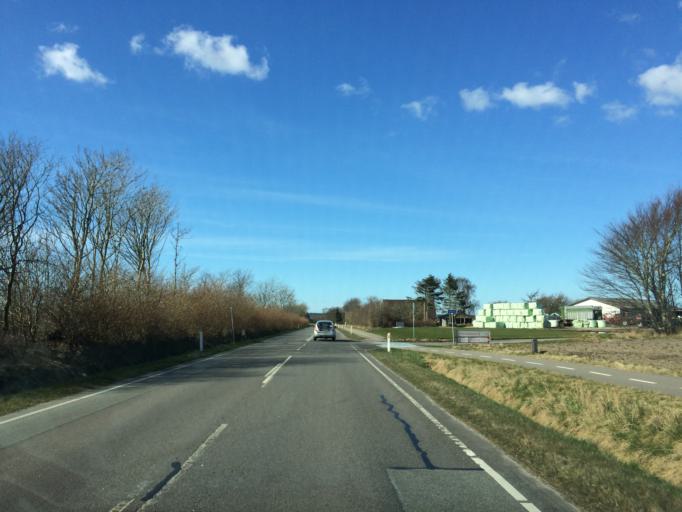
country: DK
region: South Denmark
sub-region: Varde Kommune
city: Oksbol
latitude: 55.7185
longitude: 8.2932
